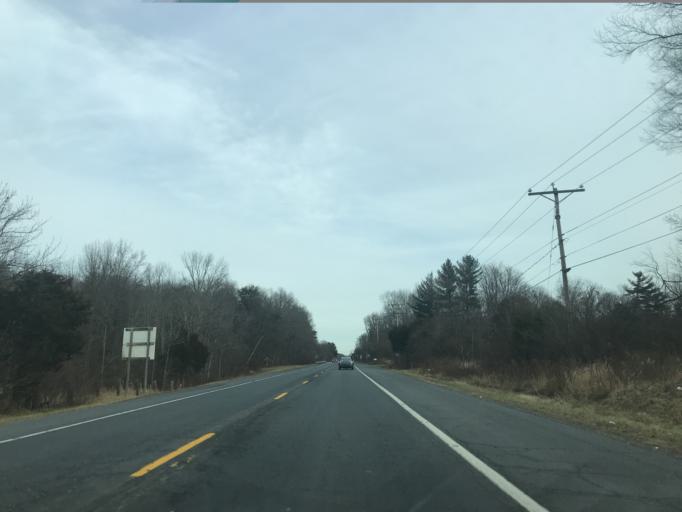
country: US
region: Maryland
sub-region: Cecil County
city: Elkton
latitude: 39.6208
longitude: -75.7890
